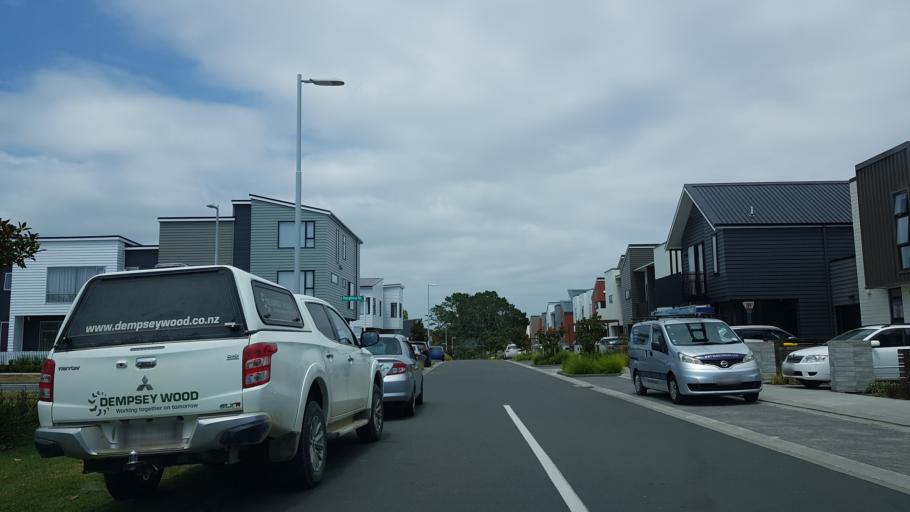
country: NZ
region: Auckland
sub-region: Auckland
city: Rosebank
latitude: -36.7936
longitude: 174.6668
